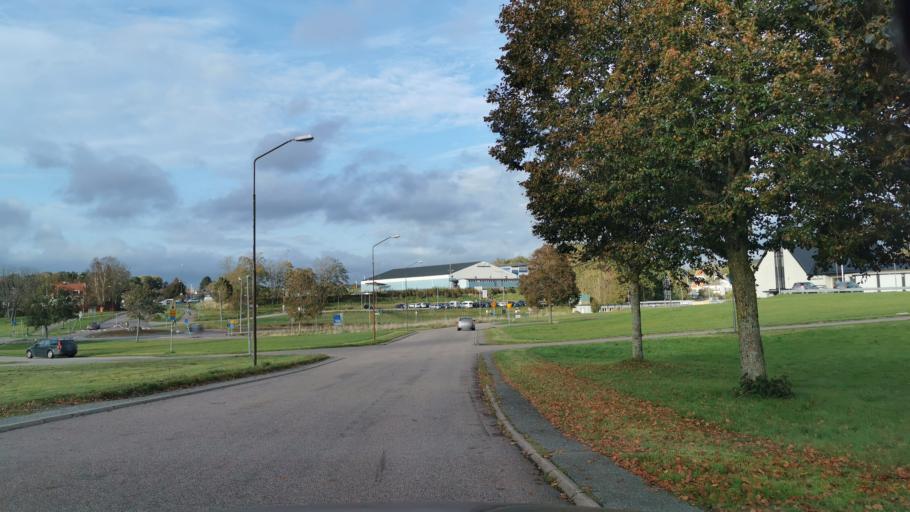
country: SE
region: Vaestra Goetaland
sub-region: Partille Kommun
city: Partille
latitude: 57.7212
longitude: 12.0779
